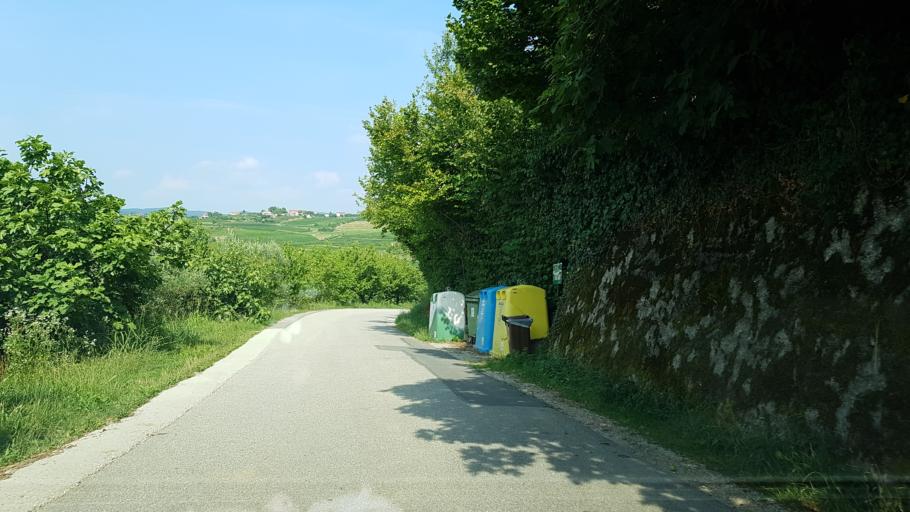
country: SI
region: Brda
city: Dobrovo
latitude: 45.9748
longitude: 13.5216
